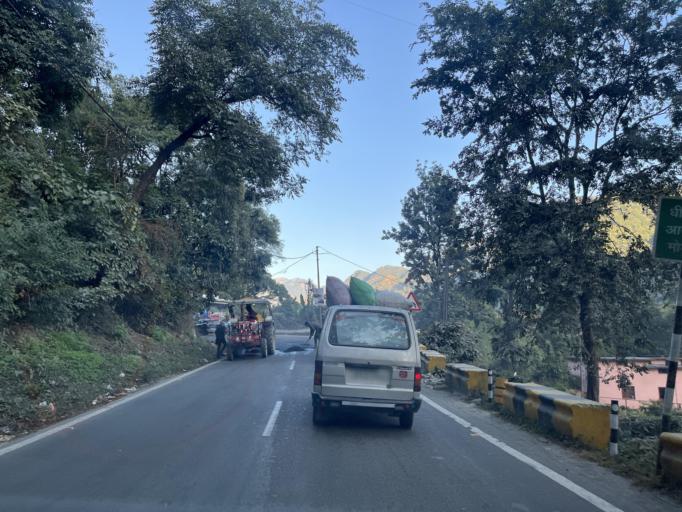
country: IN
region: Uttarakhand
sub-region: Naini Tal
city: Bhim Tal
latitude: 29.2900
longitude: 79.5462
